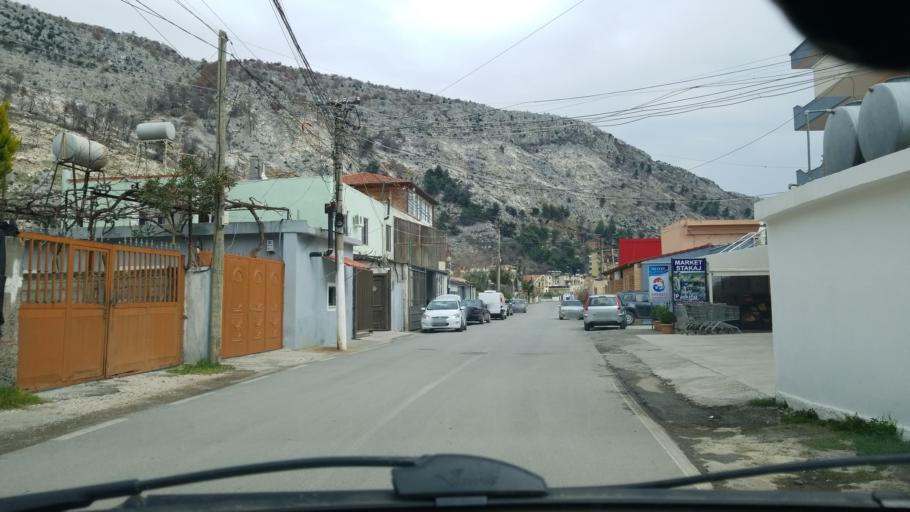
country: AL
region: Lezhe
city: Shengjin
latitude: 41.8152
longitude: 19.5862
